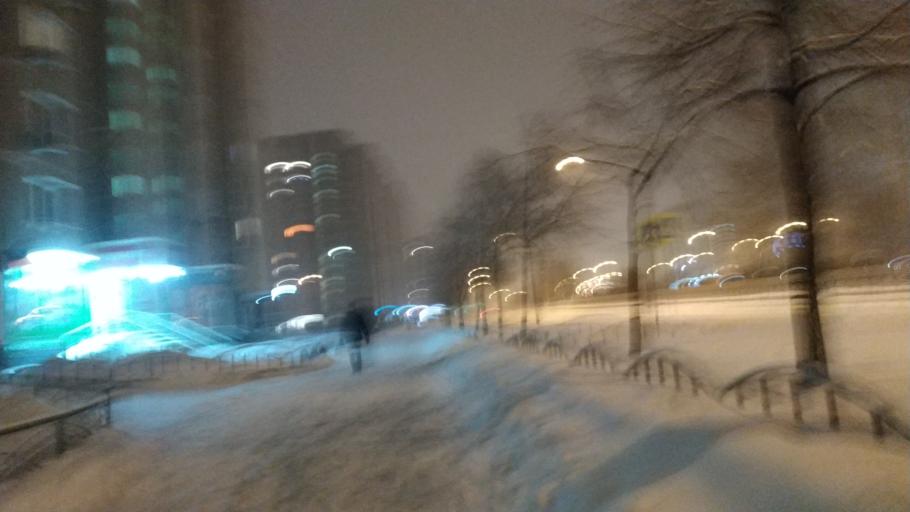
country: RU
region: Moscow
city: Zhulebino
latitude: 55.6893
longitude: 37.8600
